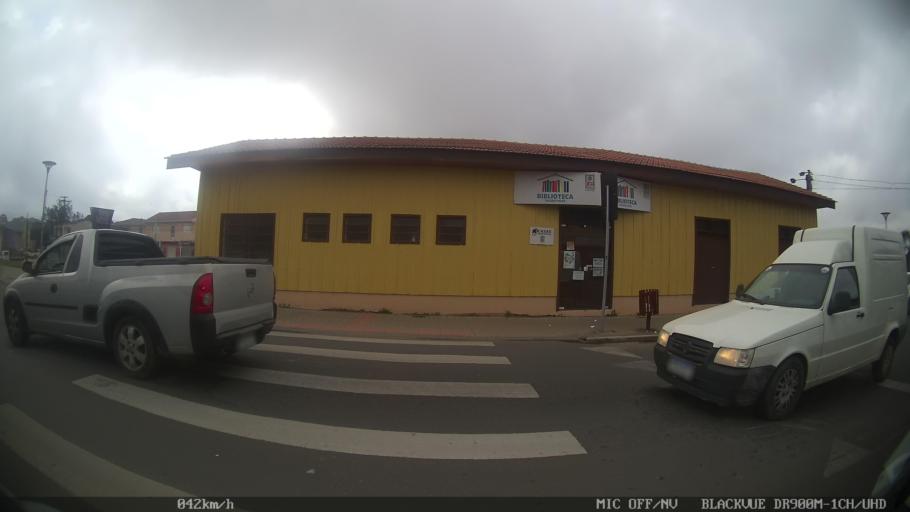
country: BR
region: Parana
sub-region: Almirante Tamandare
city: Almirante Tamandare
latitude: -25.3405
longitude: -49.2701
